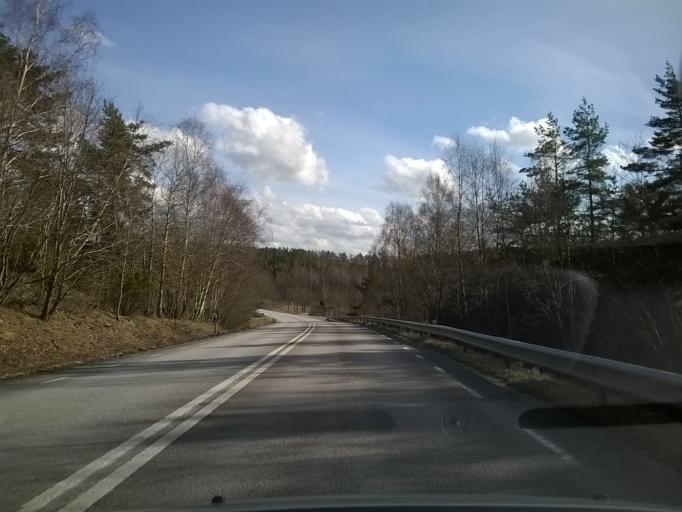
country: SE
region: Vaestra Goetaland
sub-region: Tjorns Kommun
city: Myggenas
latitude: 58.0639
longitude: 11.7178
